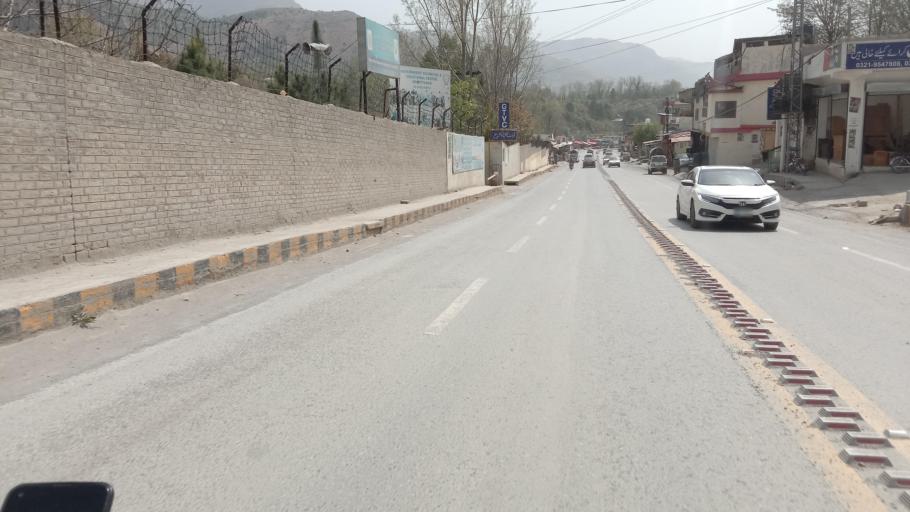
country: PK
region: Khyber Pakhtunkhwa
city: Abbottabad
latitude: 34.1552
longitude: 73.2664
